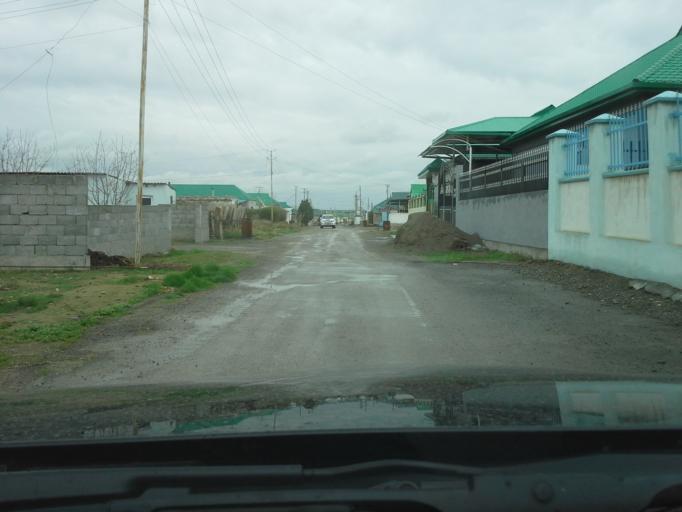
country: TM
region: Ahal
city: Abadan
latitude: 37.9697
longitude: 58.2061
